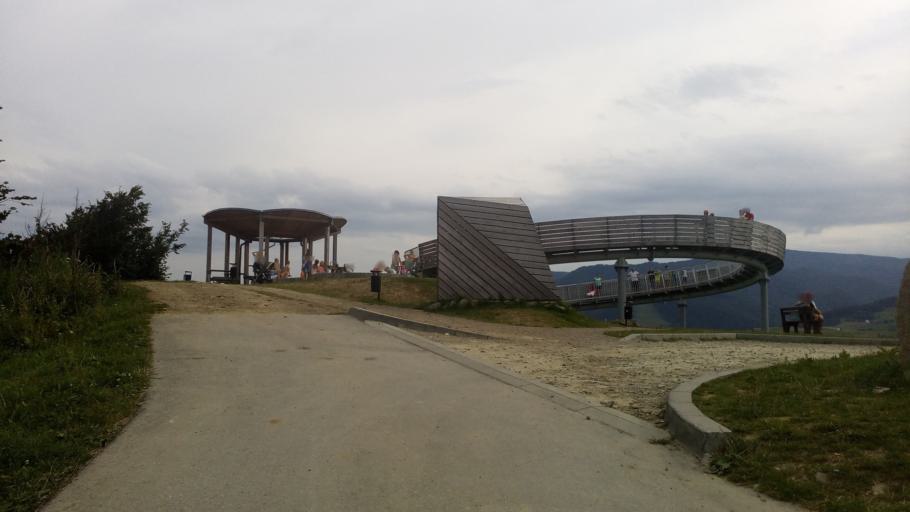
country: PL
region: Lesser Poland Voivodeship
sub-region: Powiat nowosadecki
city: Rytro
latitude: 49.5092
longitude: 20.6715
